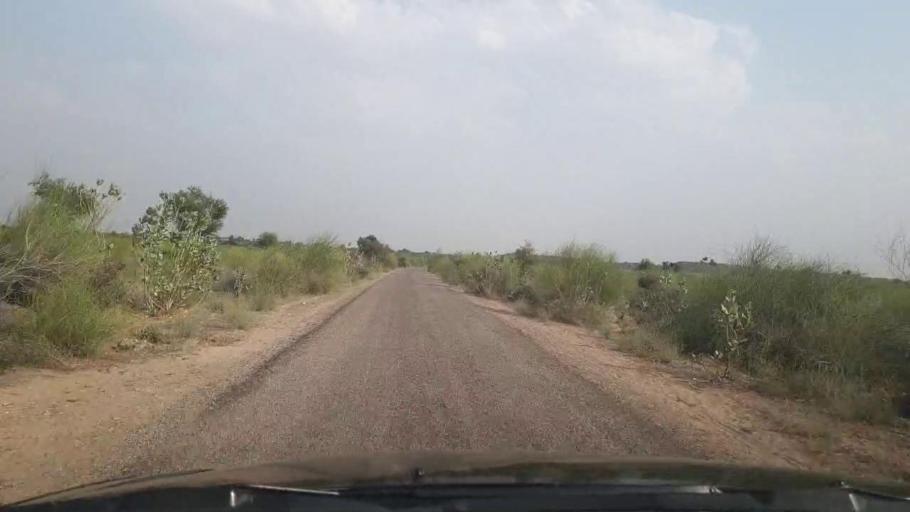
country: PK
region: Sindh
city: Islamkot
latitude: 25.0273
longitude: 70.5840
